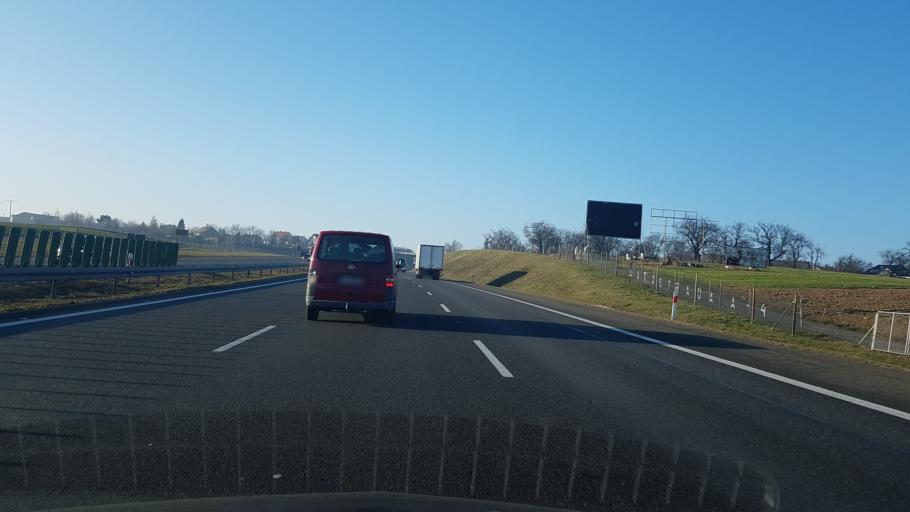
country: PL
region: Opole Voivodeship
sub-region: Powiat strzelecki
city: Lesnica
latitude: 50.4655
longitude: 18.1712
